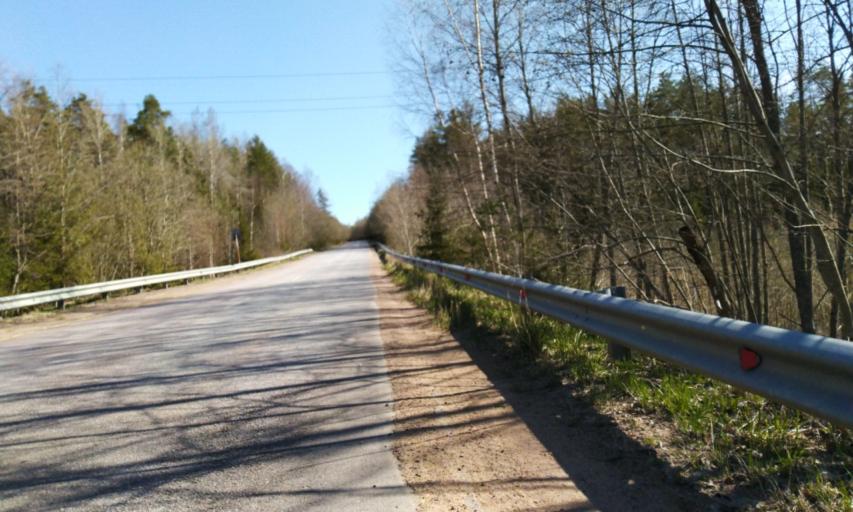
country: RU
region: Leningrad
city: Garbolovo
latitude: 60.3827
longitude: 30.4684
